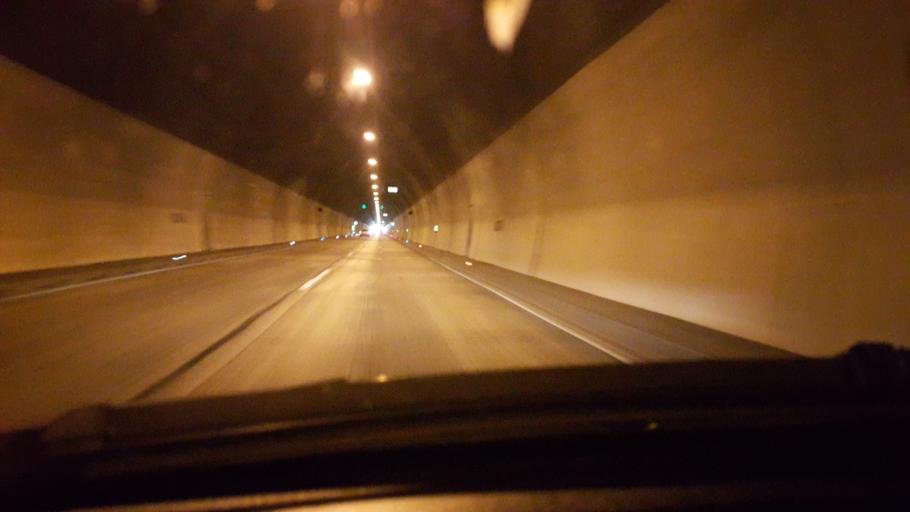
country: SI
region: Vransko
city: Vransko
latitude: 46.2109
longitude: 14.9073
